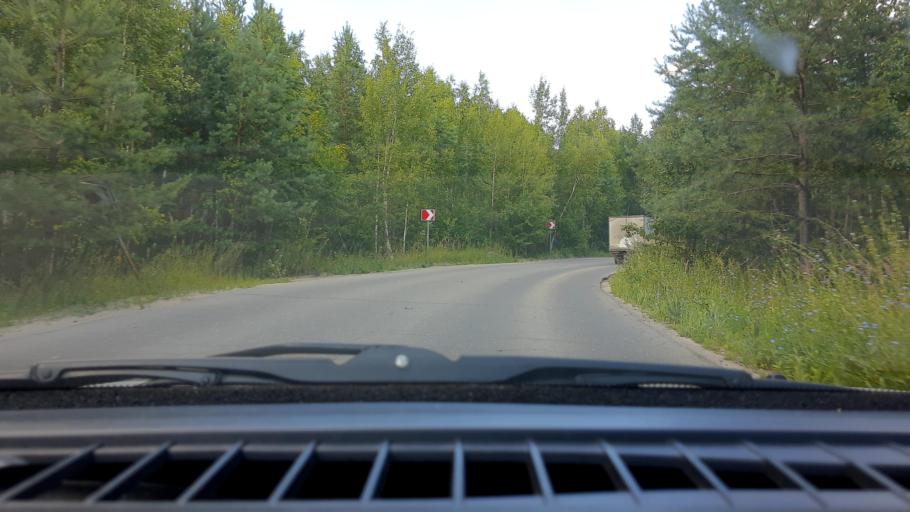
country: RU
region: Nizjnij Novgorod
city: Babino
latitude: 56.3161
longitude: 43.6235
